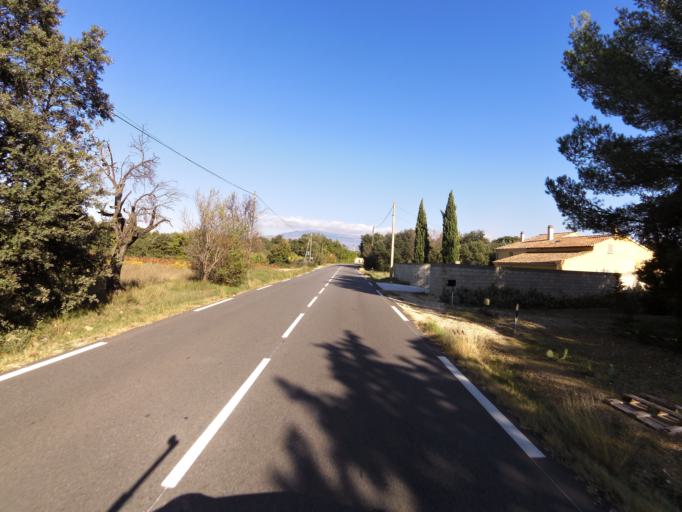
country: FR
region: Provence-Alpes-Cote d'Azur
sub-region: Departement du Vaucluse
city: Caromb
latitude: 44.0765
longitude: 5.0938
